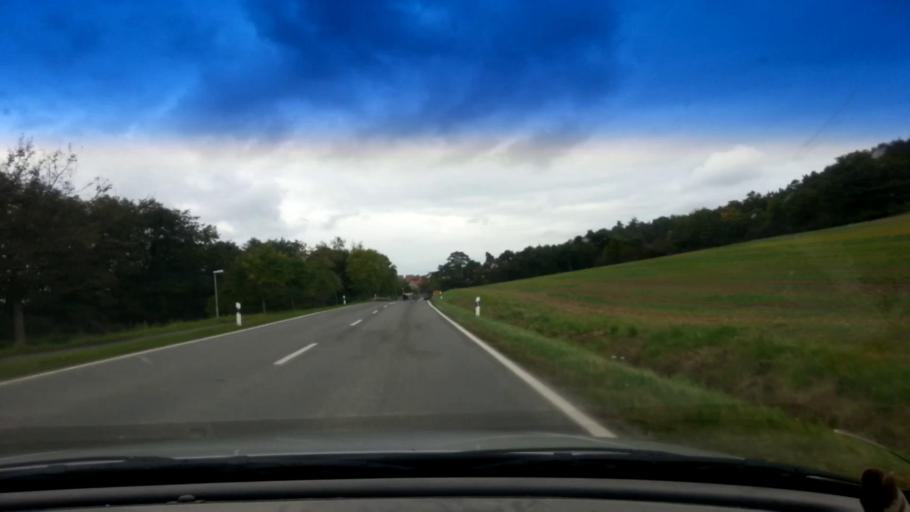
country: DE
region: Bavaria
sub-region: Upper Franconia
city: Priesendorf
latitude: 49.8995
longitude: 10.7172
